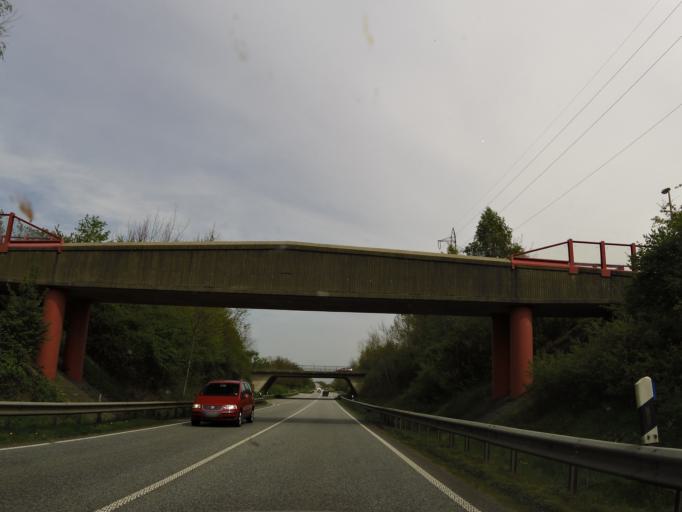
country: DE
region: Schleswig-Holstein
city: Mildstedt
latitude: 54.4714
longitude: 9.0794
